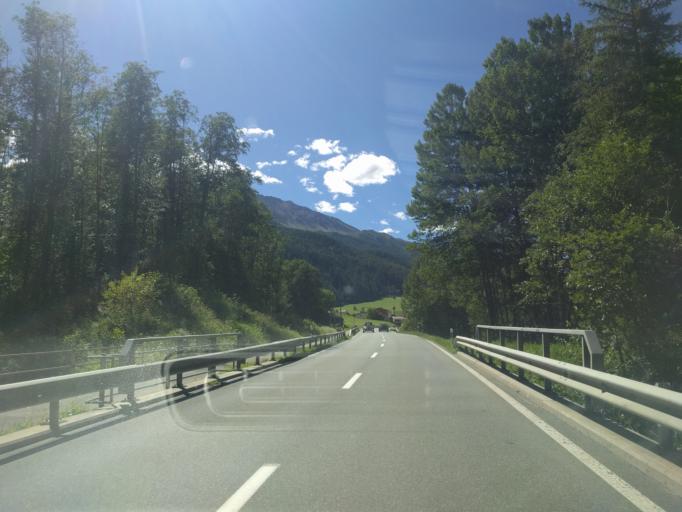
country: IT
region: Trentino-Alto Adige
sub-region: Bolzano
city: Tubre
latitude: 46.6003
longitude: 10.4154
